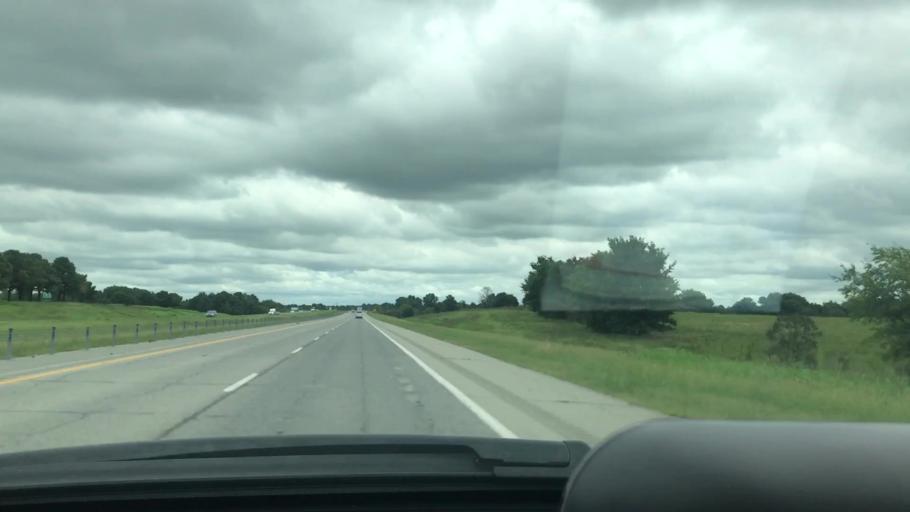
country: US
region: Oklahoma
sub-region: McIntosh County
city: Checotah
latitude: 35.5455
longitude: -95.5016
